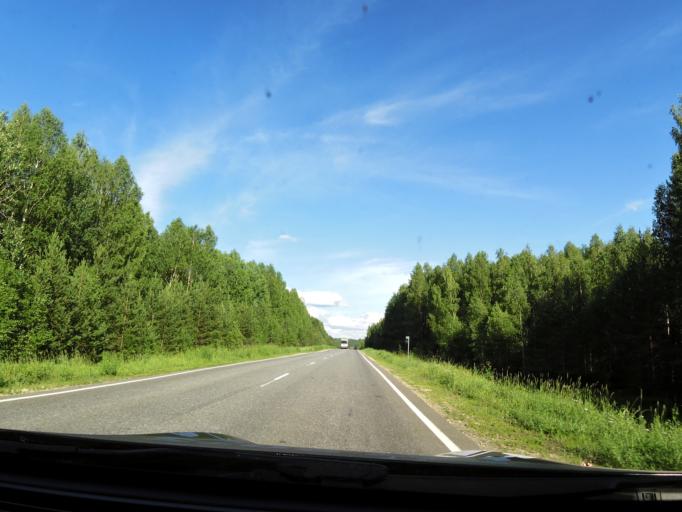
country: RU
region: Kirov
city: Chernaya Kholunitsa
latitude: 58.8280
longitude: 51.7728
